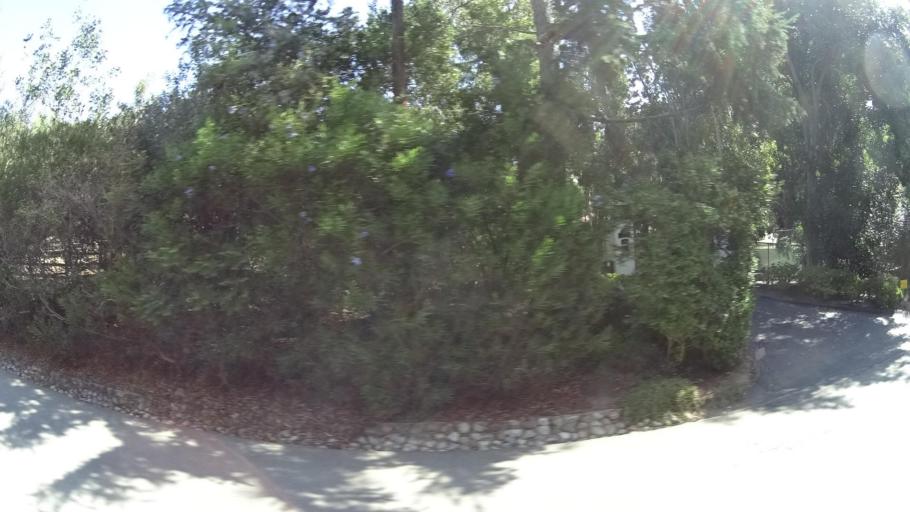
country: US
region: California
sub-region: San Diego County
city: Rancho Santa Fe
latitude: 33.0113
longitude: -117.2043
